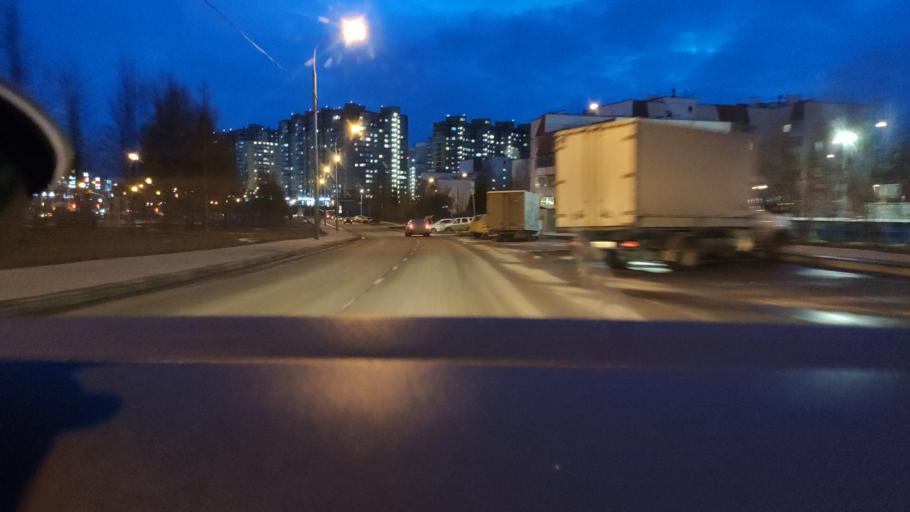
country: RU
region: Moskovskaya
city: Kommunarka
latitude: 55.5291
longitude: 37.5182
